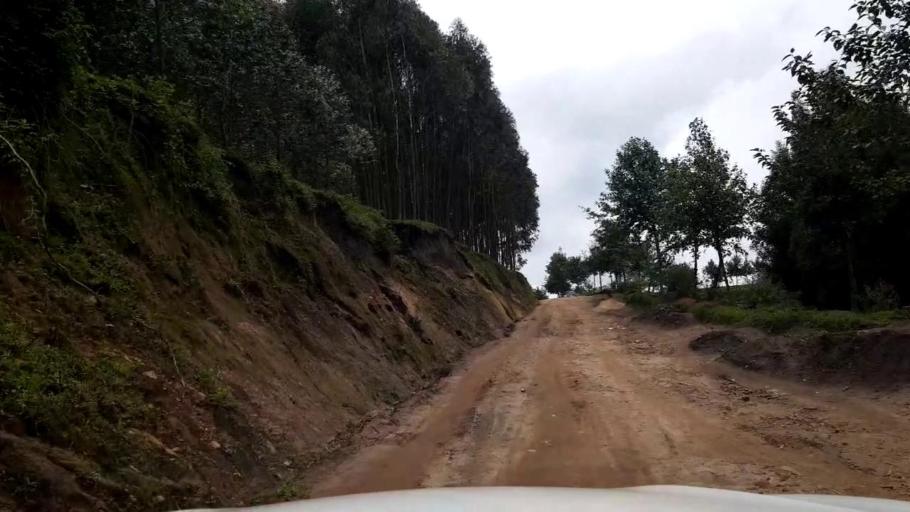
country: RW
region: Western Province
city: Kibuye
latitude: -1.9514
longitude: 29.4102
